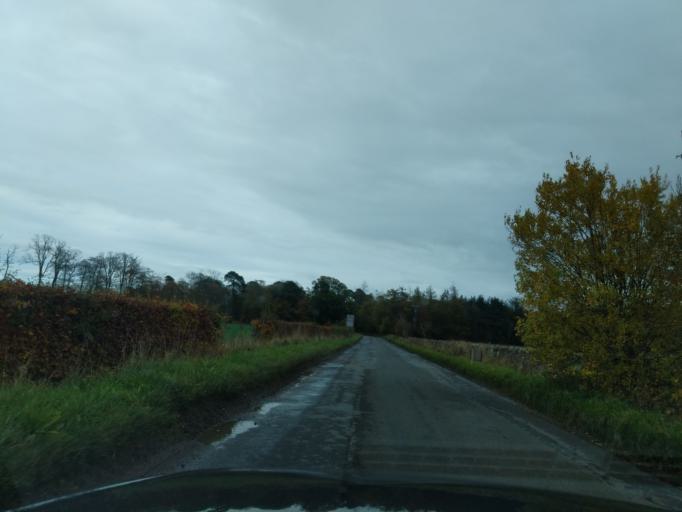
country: GB
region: Scotland
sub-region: Fife
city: Saint Andrews
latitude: 56.2879
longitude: -2.8251
